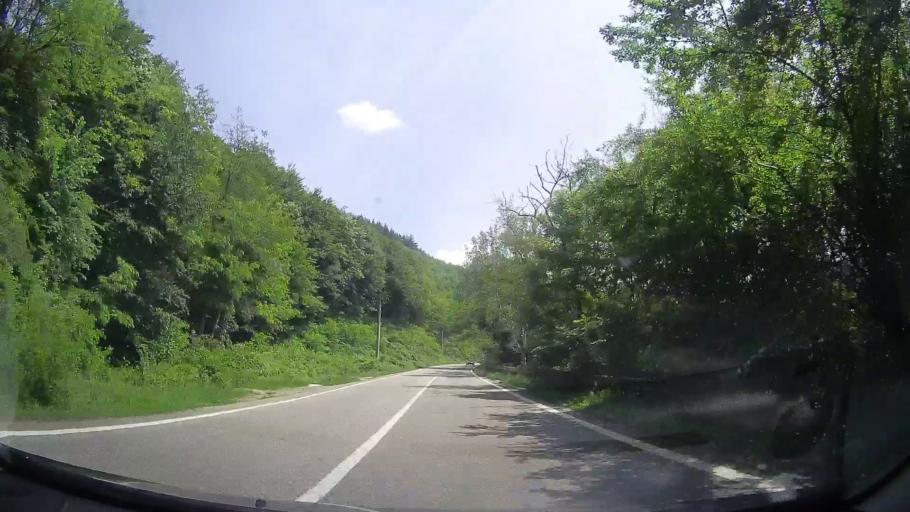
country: RO
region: Valcea
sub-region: Oras Calimanesti
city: Calimanesti
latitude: 45.2696
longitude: 24.3212
